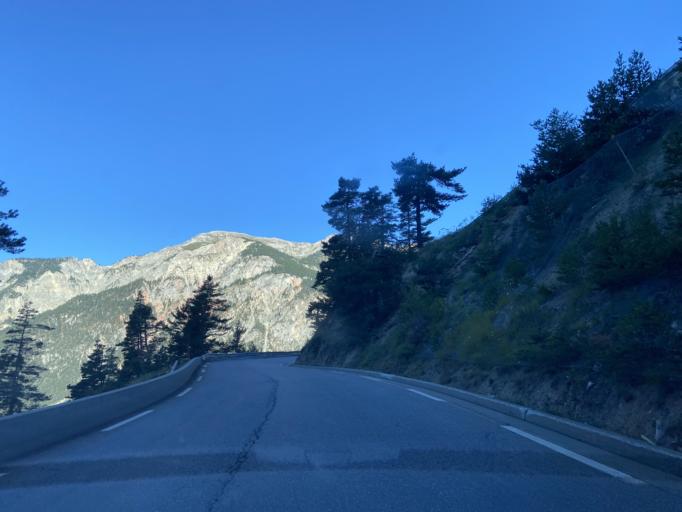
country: FR
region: Provence-Alpes-Cote d'Azur
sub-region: Departement des Hautes-Alpes
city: Briancon
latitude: 44.9287
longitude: 6.6912
